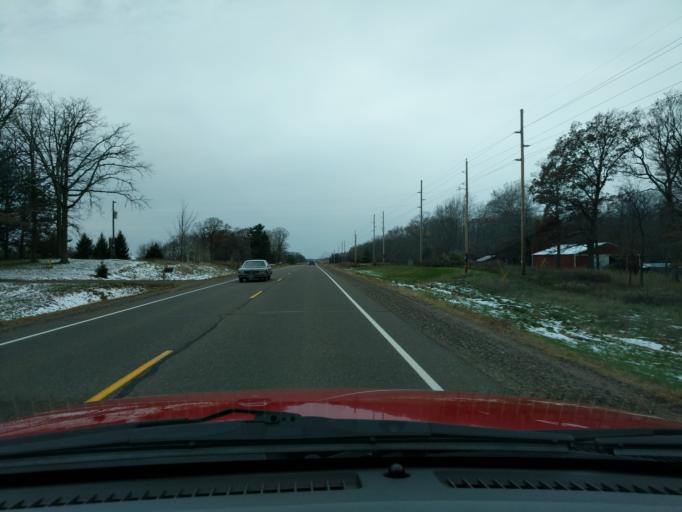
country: US
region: Wisconsin
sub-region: Washburn County
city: Shell Lake
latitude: 45.8153
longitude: -92.0357
